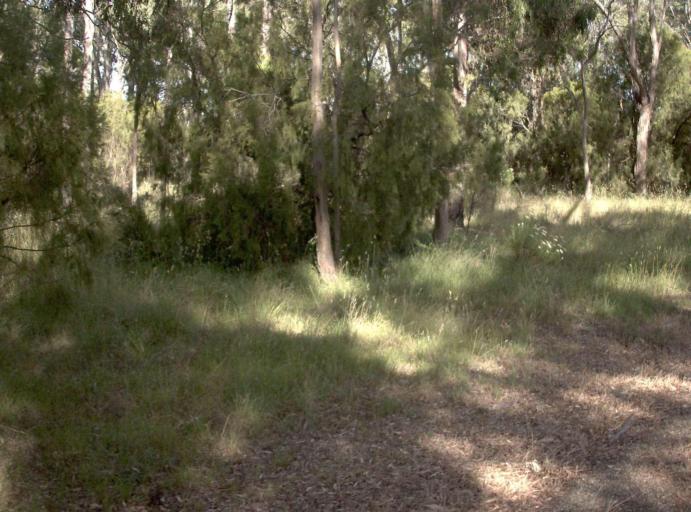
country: AU
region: Victoria
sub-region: East Gippsland
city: Lakes Entrance
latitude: -37.8007
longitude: 147.8353
